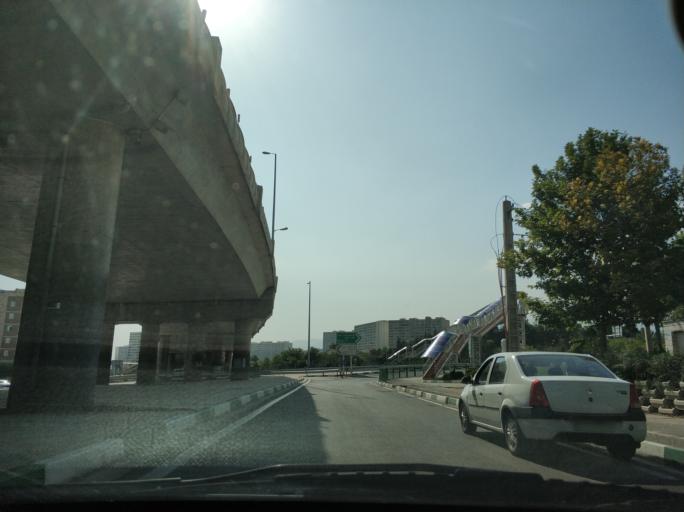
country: IR
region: Tehran
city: Tajrish
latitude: 35.7592
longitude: 51.5372
